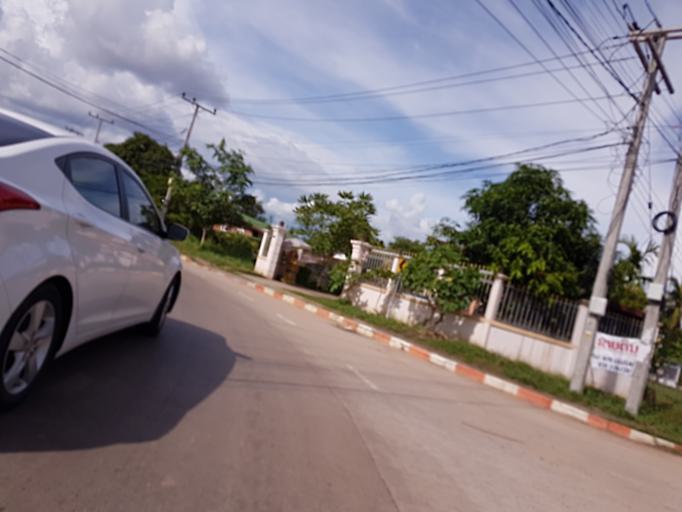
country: LA
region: Vientiane
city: Vientiane
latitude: 17.9233
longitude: 102.6247
